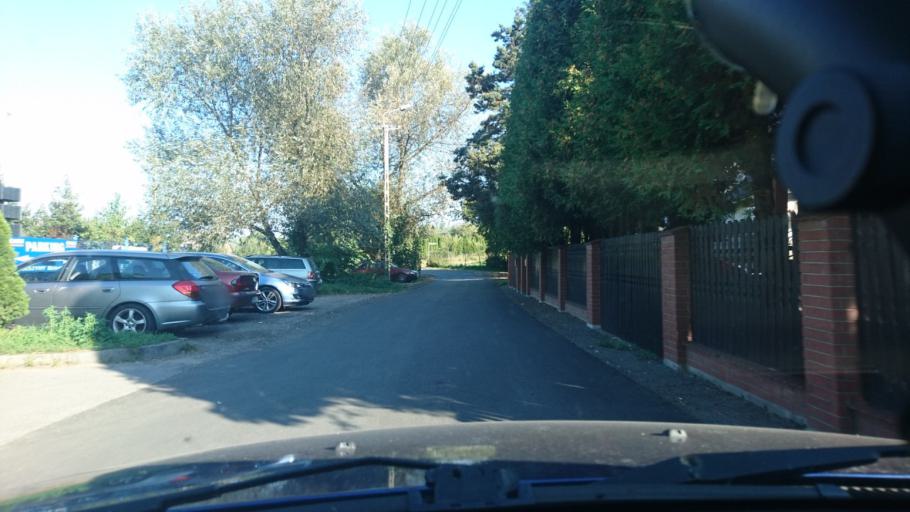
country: PL
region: Silesian Voivodeship
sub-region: Bielsko-Biala
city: Bielsko-Biala
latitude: 49.8462
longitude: 19.0546
